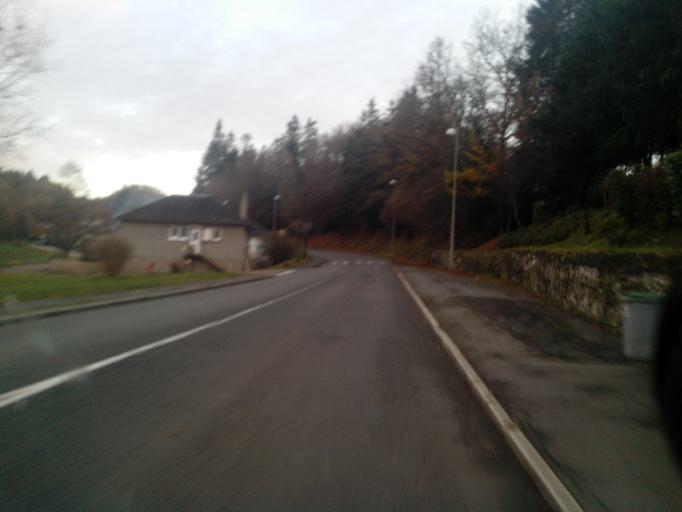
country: FR
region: Limousin
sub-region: Departement de la Correze
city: Meymac
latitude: 45.5337
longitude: 2.1537
